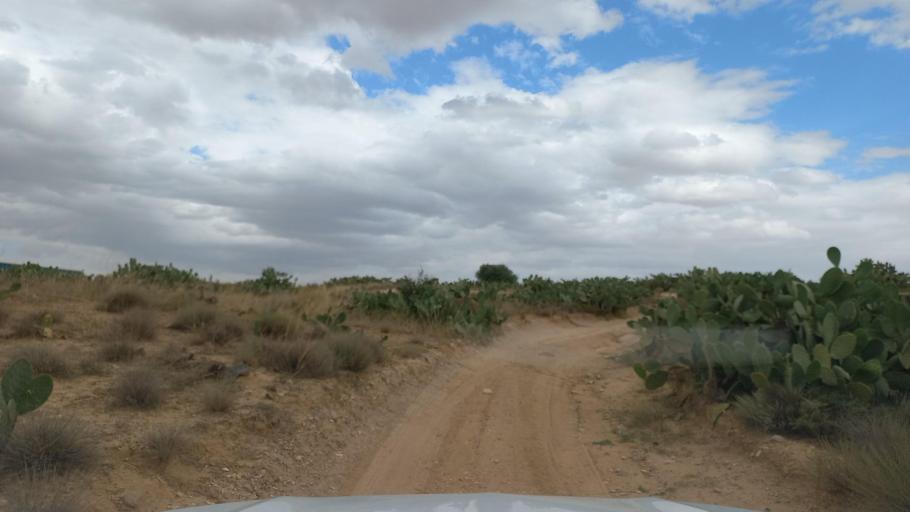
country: TN
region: Al Qasrayn
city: Sbiba
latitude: 35.3788
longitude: 9.1284
